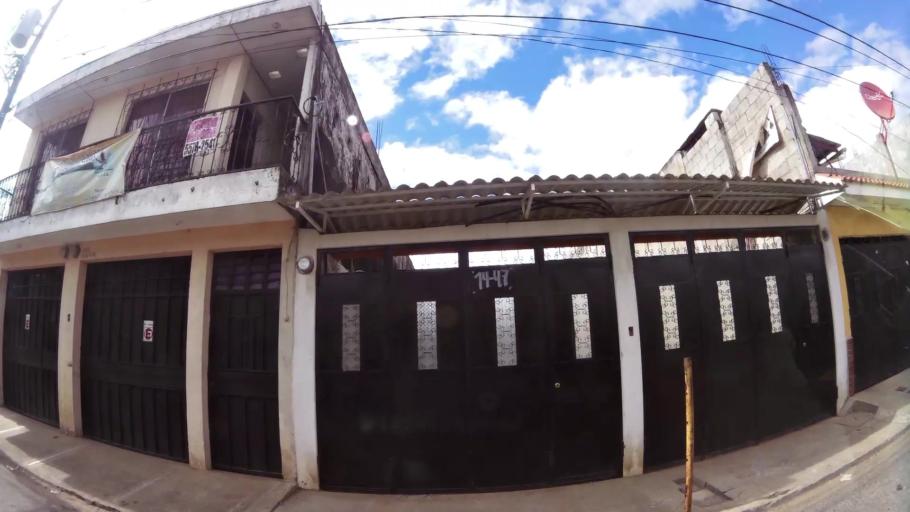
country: GT
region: Guatemala
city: Guatemala City
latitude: 14.6818
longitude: -90.5450
